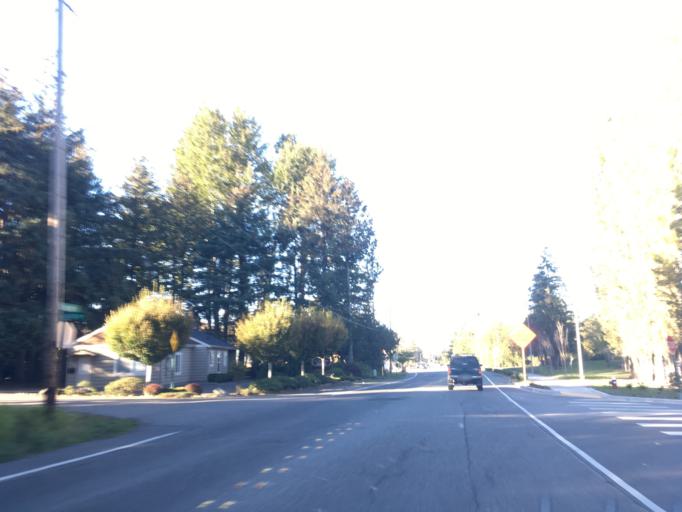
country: US
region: Washington
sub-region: Whatcom County
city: Bellingham
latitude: 48.7351
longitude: -122.4660
